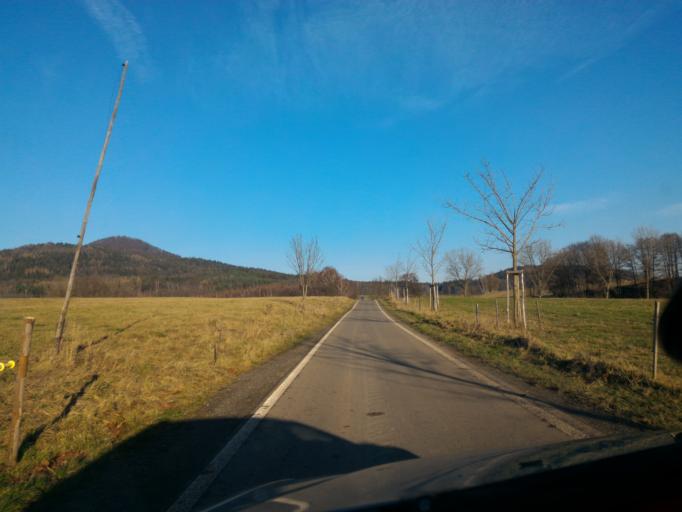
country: CZ
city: Jablonne v Podjestedi
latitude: 50.7929
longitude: 14.7389
